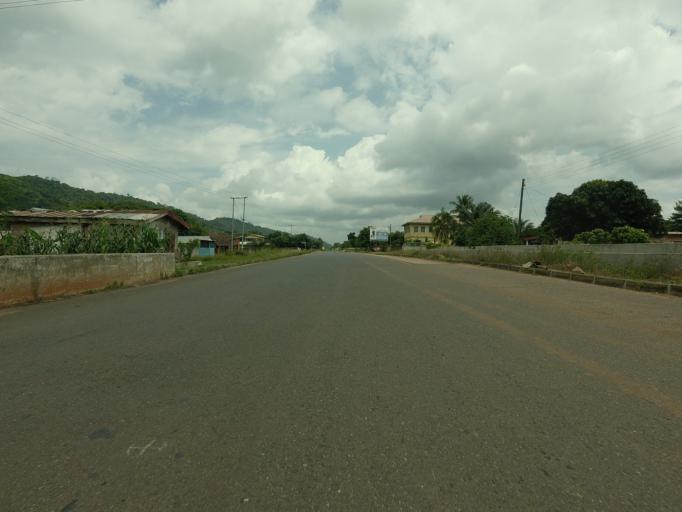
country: GH
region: Volta
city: Ho
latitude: 6.5008
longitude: 0.2054
